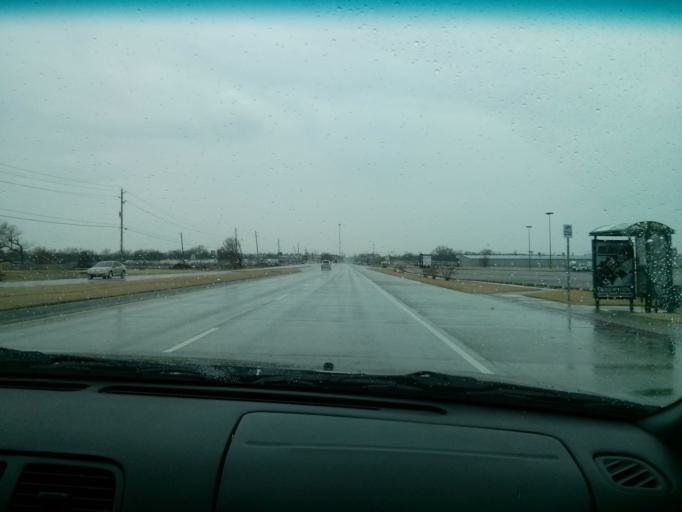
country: US
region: Oklahoma
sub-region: Tulsa County
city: Owasso
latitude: 36.1608
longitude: -95.8632
